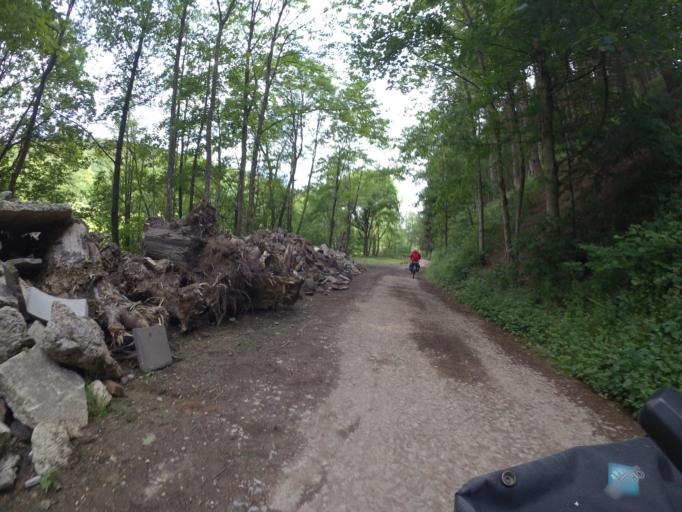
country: DE
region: North Rhine-Westphalia
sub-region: Regierungsbezirk Koln
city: Hellenthal
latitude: 50.4776
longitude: 6.4269
